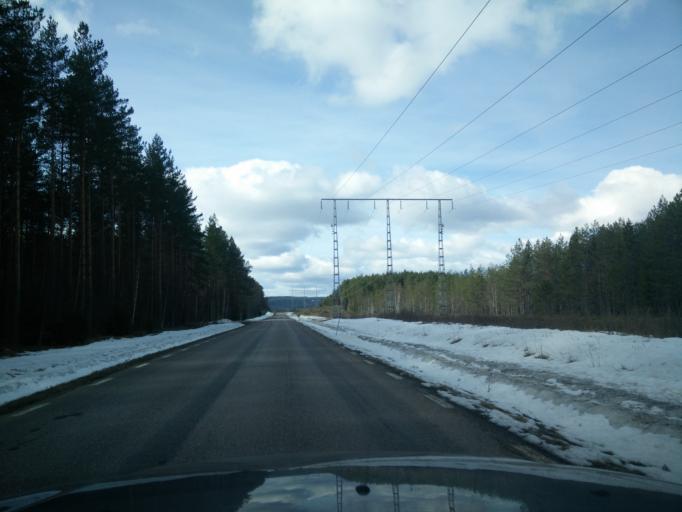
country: SE
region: Vaermland
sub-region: Hagfors Kommun
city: Hagfors
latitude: 60.0392
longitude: 13.5429
